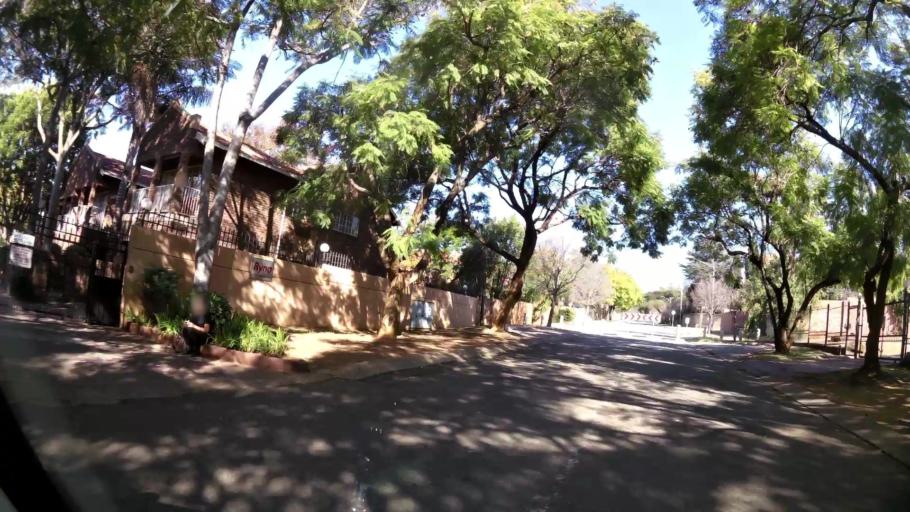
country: ZA
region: Gauteng
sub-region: City of Tshwane Metropolitan Municipality
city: Pretoria
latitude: -25.7852
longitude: 28.2670
